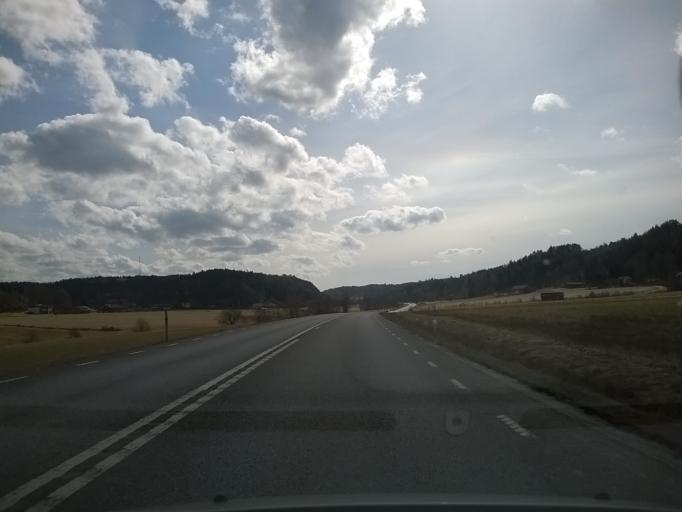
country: SE
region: Vaestra Goetaland
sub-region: Orust
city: Henan
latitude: 58.1607
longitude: 11.7060
